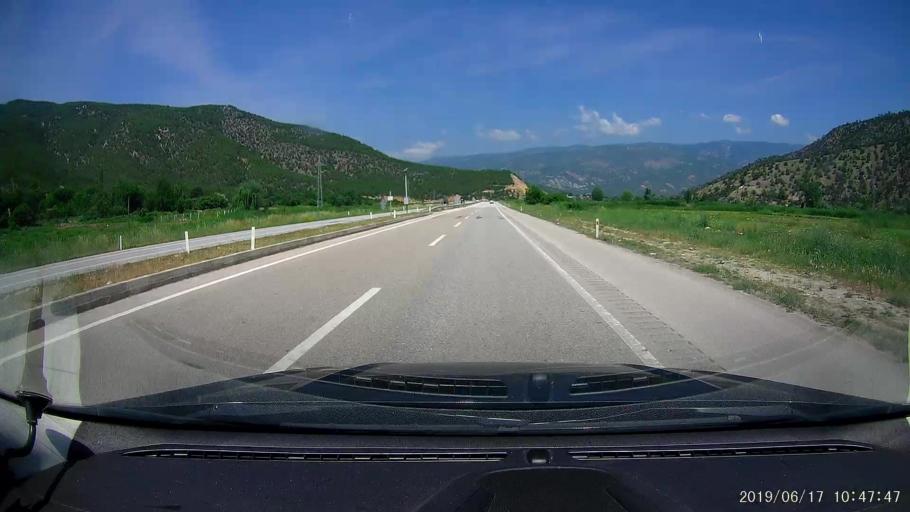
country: TR
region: Corum
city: Hacihamza
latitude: 41.0805
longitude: 34.4425
